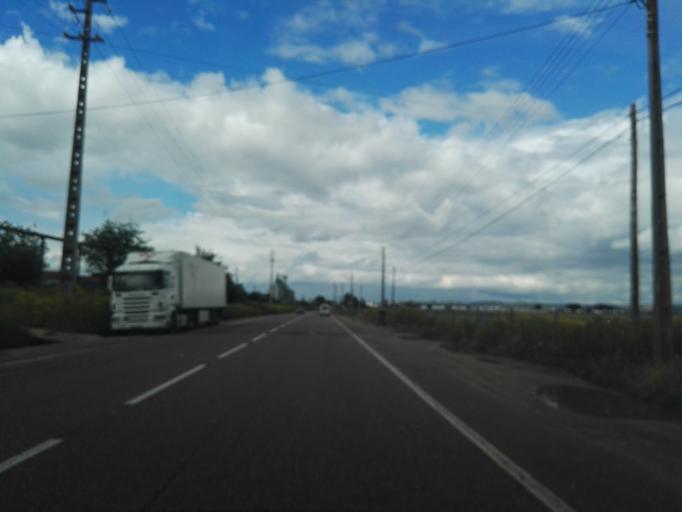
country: PT
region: Santarem
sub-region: Torres Novas
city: Riachos
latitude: 39.4362
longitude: -8.4969
